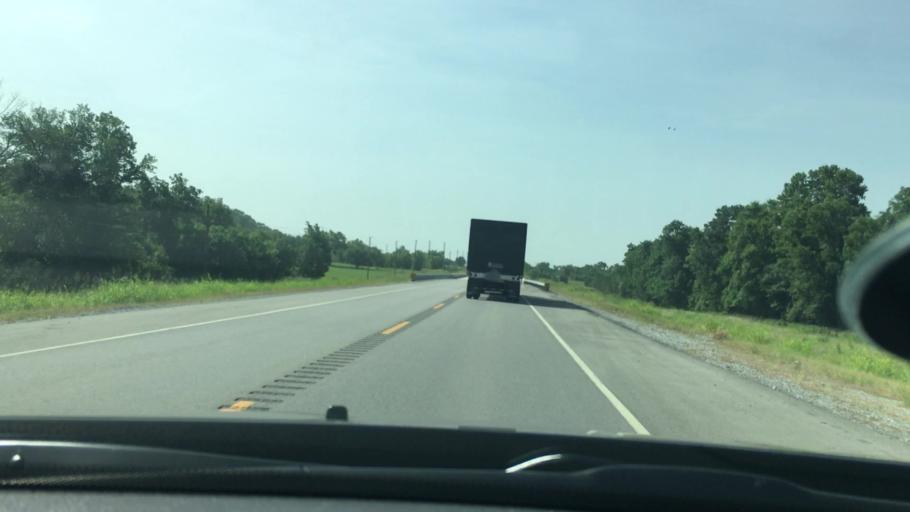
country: US
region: Oklahoma
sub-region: Coal County
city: Coalgate
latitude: 34.4472
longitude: -96.2077
